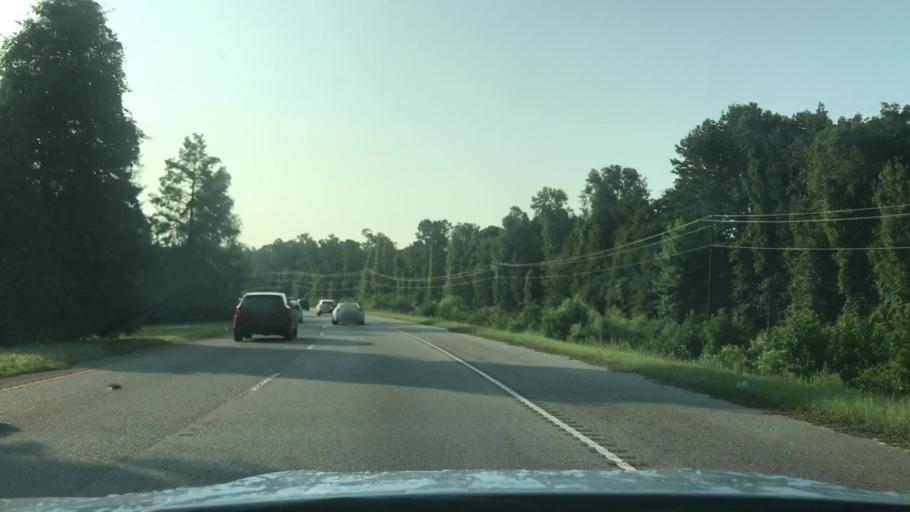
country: US
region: South Carolina
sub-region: Charleston County
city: Shell Point
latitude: 32.8120
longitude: -80.0579
